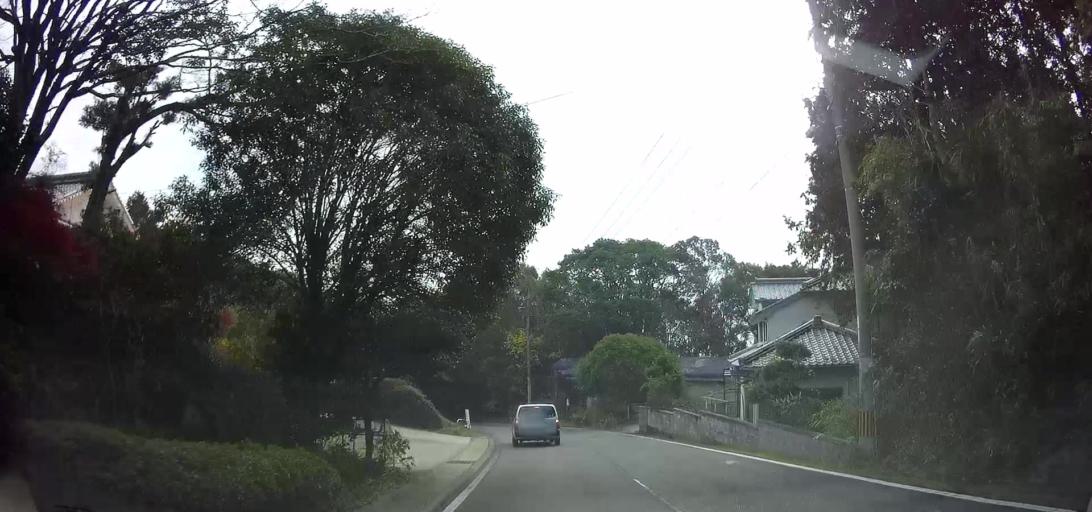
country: JP
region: Nagasaki
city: Shimabara
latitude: 32.6850
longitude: 130.2708
